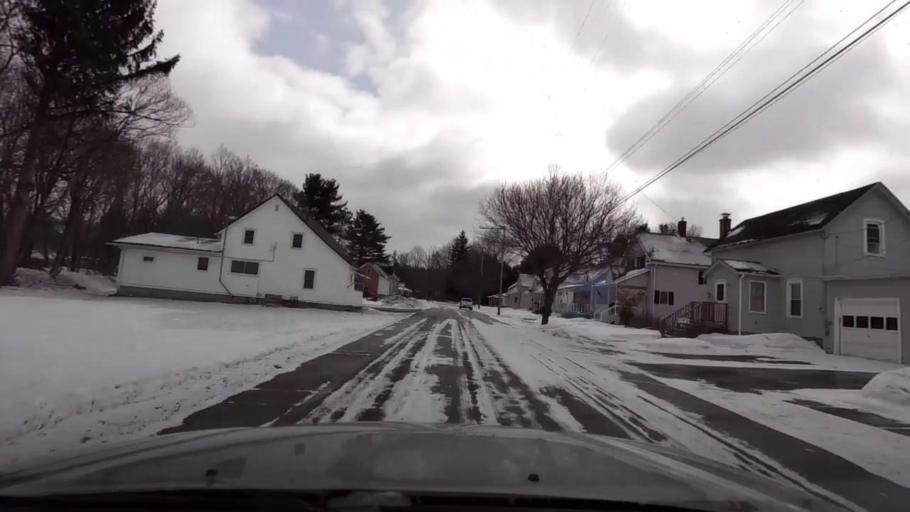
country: US
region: New York
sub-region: Allegany County
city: Cuba
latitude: 42.2951
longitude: -78.3536
